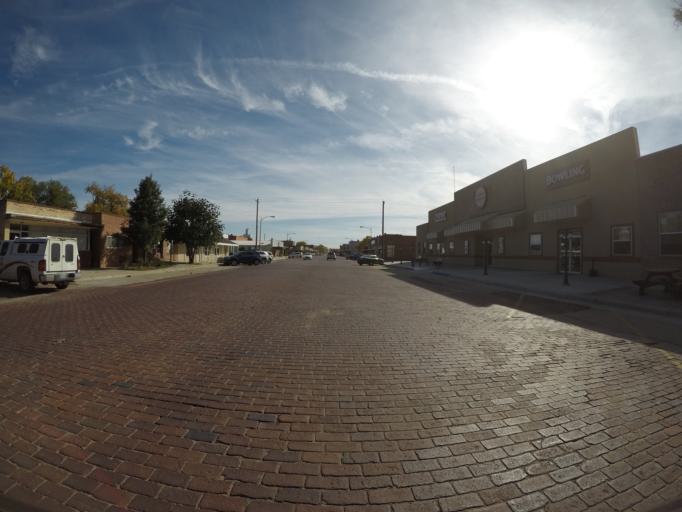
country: US
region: Kansas
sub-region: Decatur County
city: Oberlin
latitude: 39.8224
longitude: -100.5291
